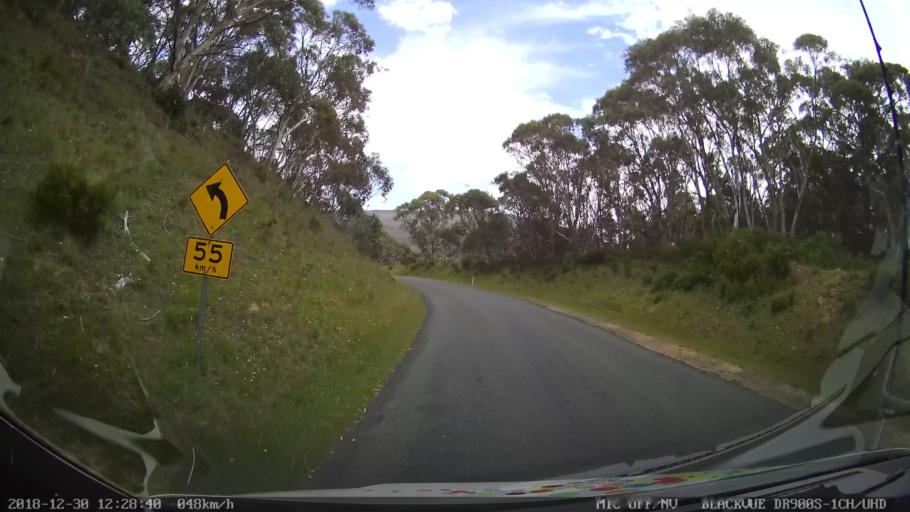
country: AU
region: New South Wales
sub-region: Snowy River
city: Jindabyne
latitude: -36.3246
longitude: 148.4835
